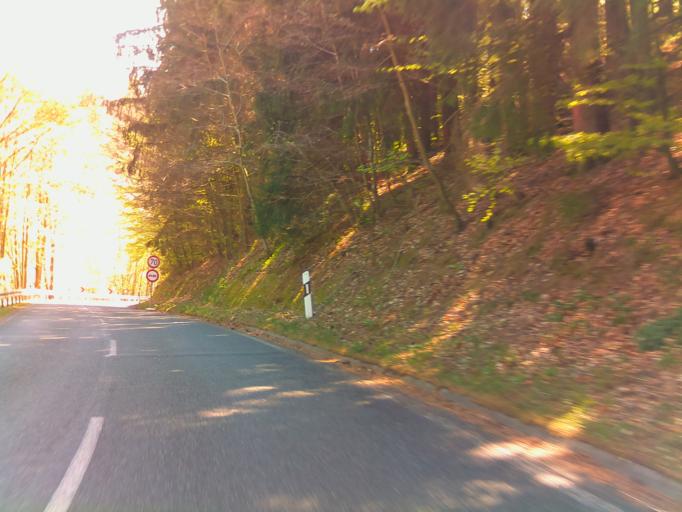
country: DE
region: Thuringia
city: Sankt Kilian
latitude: 50.5076
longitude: 10.8333
